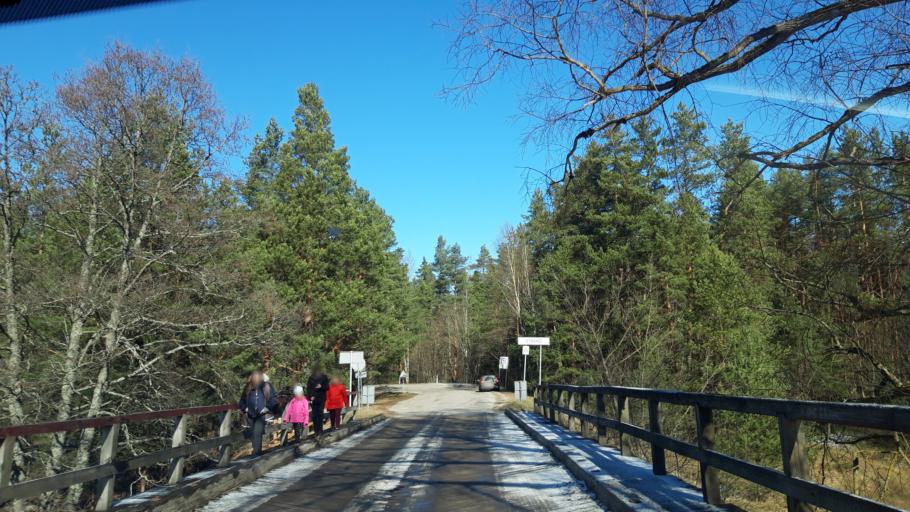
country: LV
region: Strenci
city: Strenci
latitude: 57.6189
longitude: 25.7015
